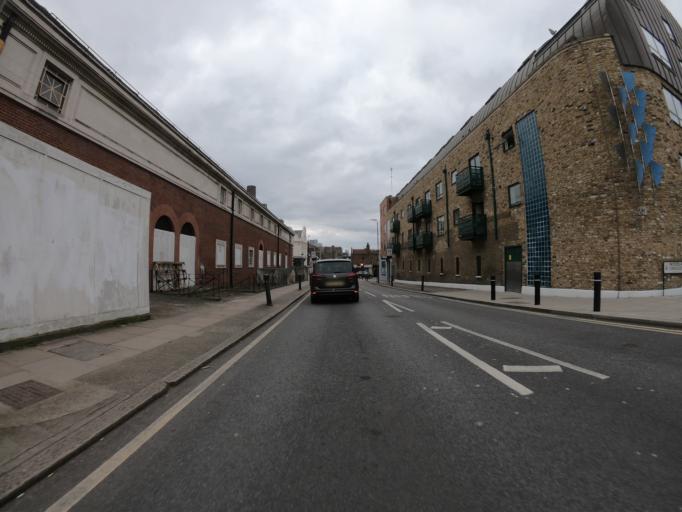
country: GB
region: England
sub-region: Greater London
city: Blackheath
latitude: 51.4834
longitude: 0.0012
